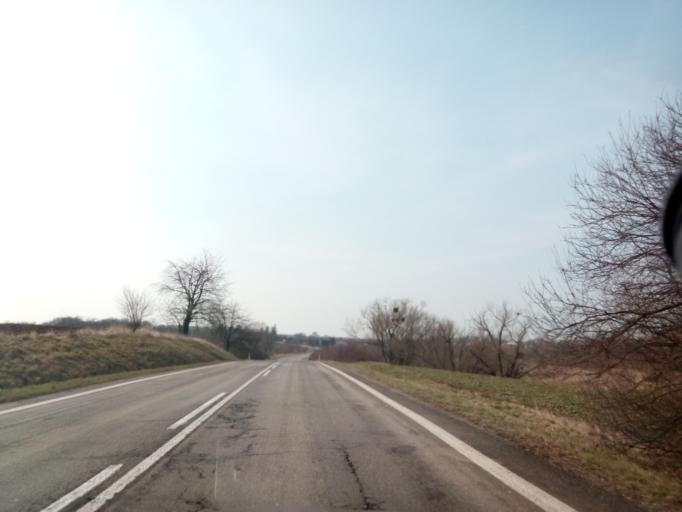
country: SK
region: Kosicky
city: Trebisov
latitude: 48.5291
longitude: 21.6706
